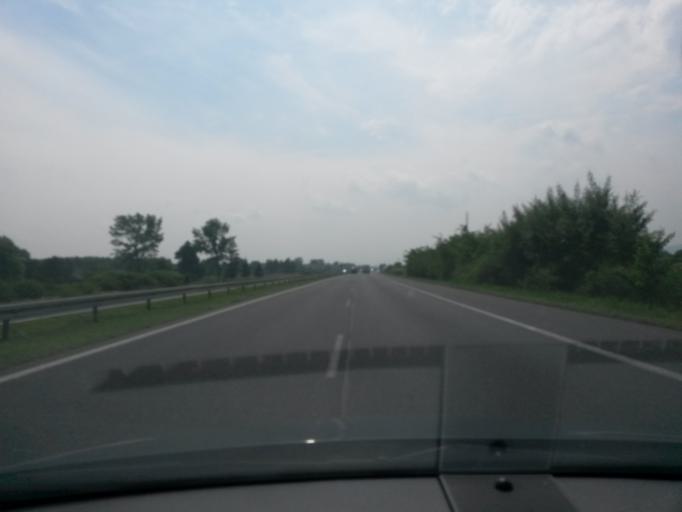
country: PL
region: Lodz Voivodeship
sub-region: Powiat radomszczanski
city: Kamiensk
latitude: 51.2392
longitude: 19.5193
